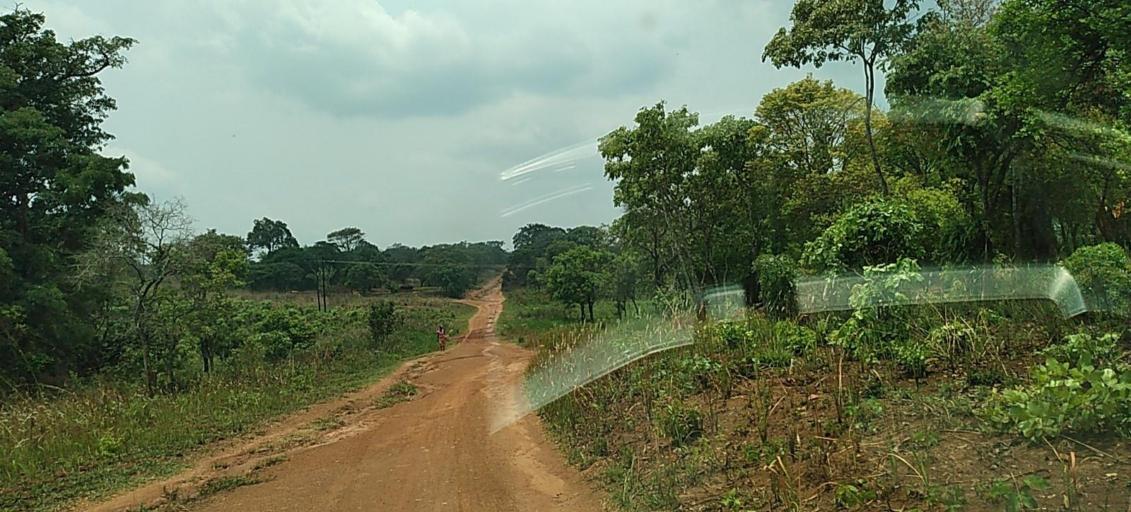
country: ZM
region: North-Western
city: Mwinilunga
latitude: -11.5370
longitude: 24.7830
